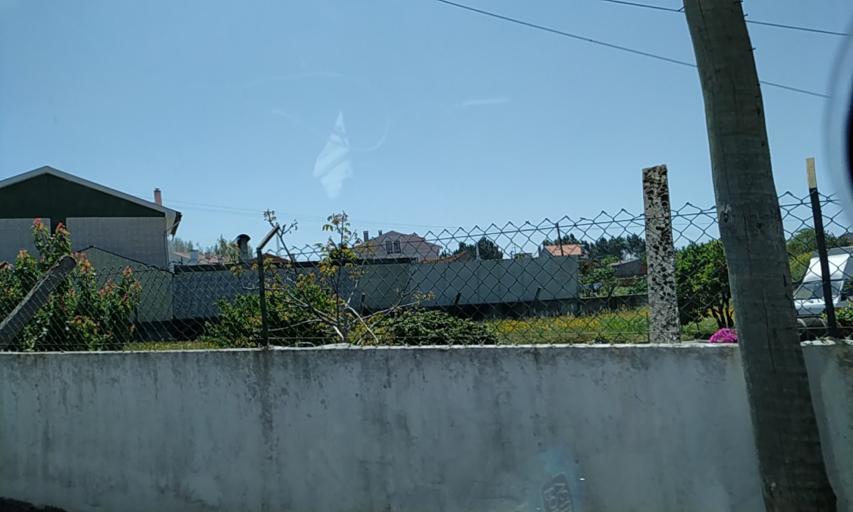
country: PT
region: Aveiro
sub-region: Aveiro
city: Aveiro
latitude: 40.6467
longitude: -8.6183
